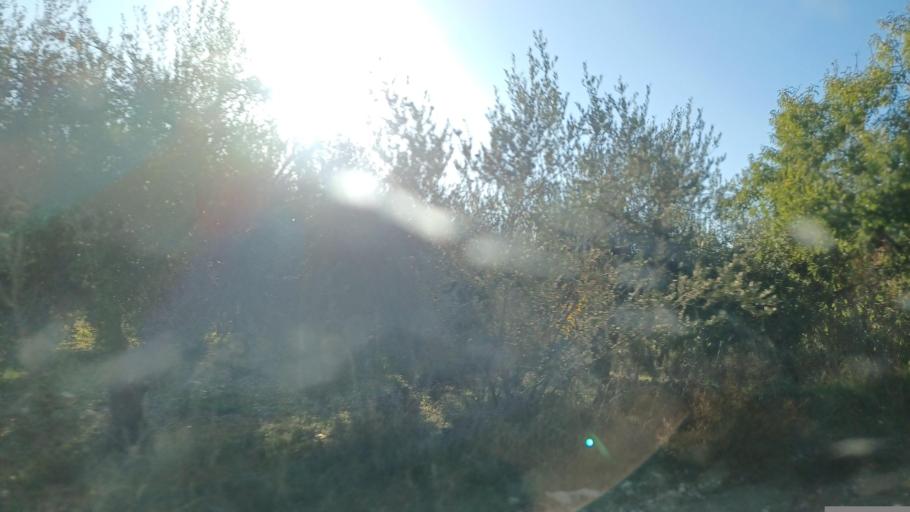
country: CY
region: Pafos
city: Mesogi
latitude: 34.9321
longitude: 32.5668
